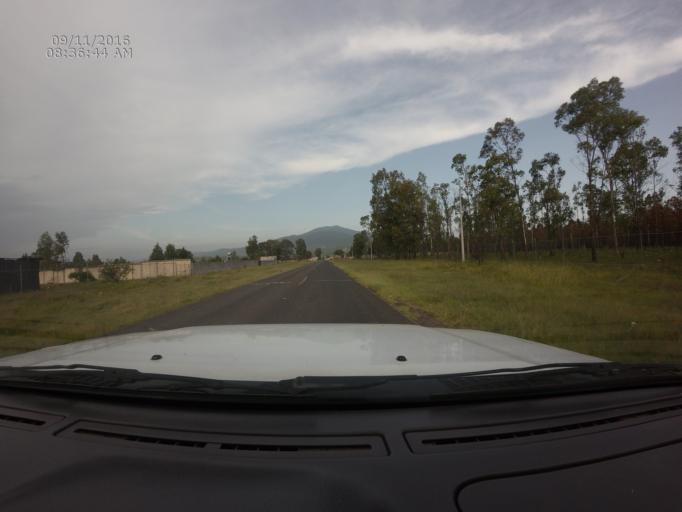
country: MX
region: Michoacan
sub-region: Morelia
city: La Mintzita (Piedra Dura)
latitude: 19.6226
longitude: -101.2689
